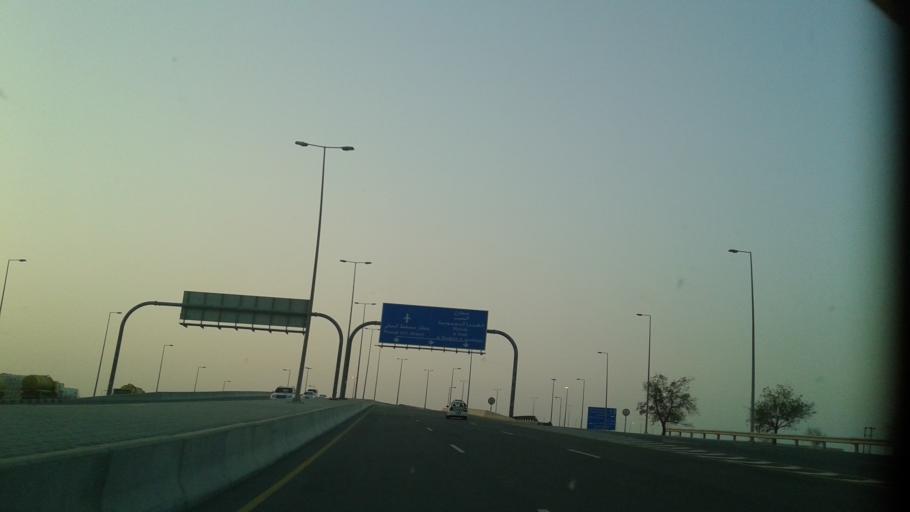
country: OM
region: Muhafazat Masqat
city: Bawshar
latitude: 23.5681
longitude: 58.3358
